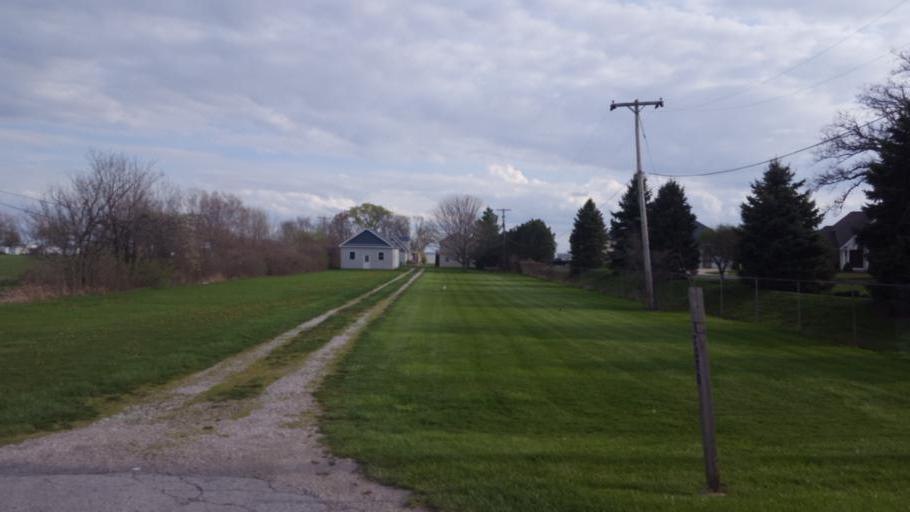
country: US
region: Ohio
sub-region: Erie County
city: Sandusky
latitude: 41.5074
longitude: -82.7985
